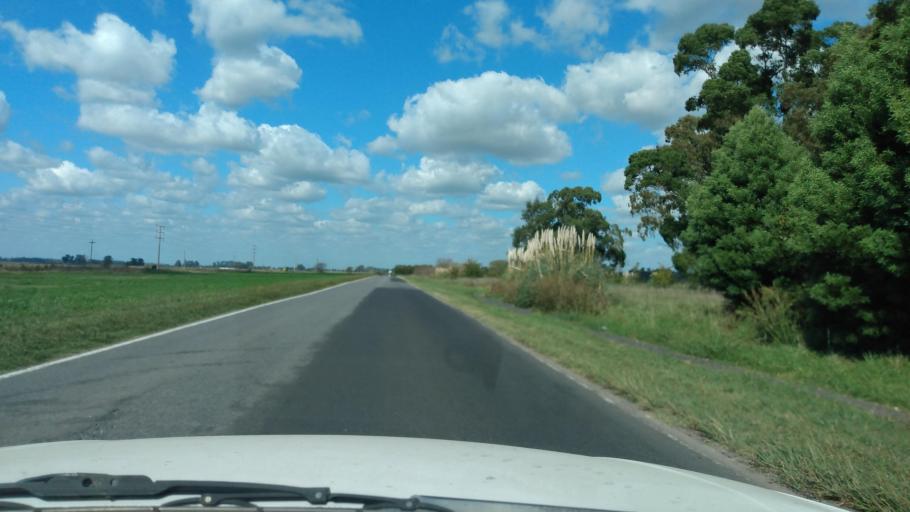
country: AR
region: Buenos Aires
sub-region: Partido de Navarro
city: Navarro
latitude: -34.9048
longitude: -59.3331
